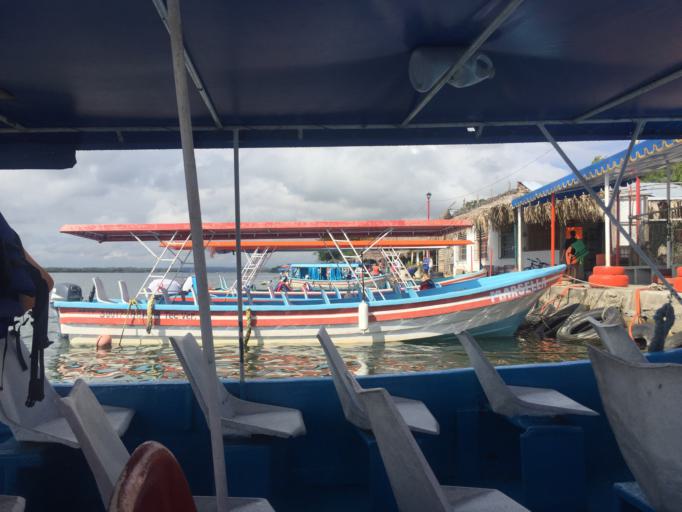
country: MX
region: Veracruz
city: Tecolutla
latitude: 20.4745
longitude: -97.0084
